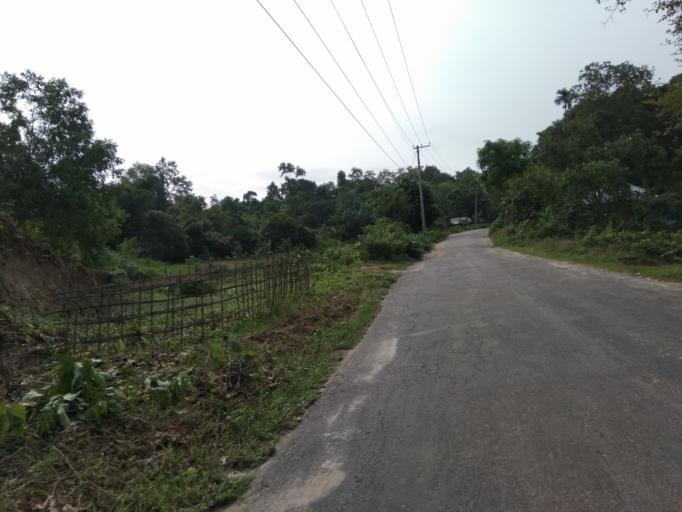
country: BD
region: Chittagong
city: Khagrachhari
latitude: 23.0355
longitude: 92.0064
